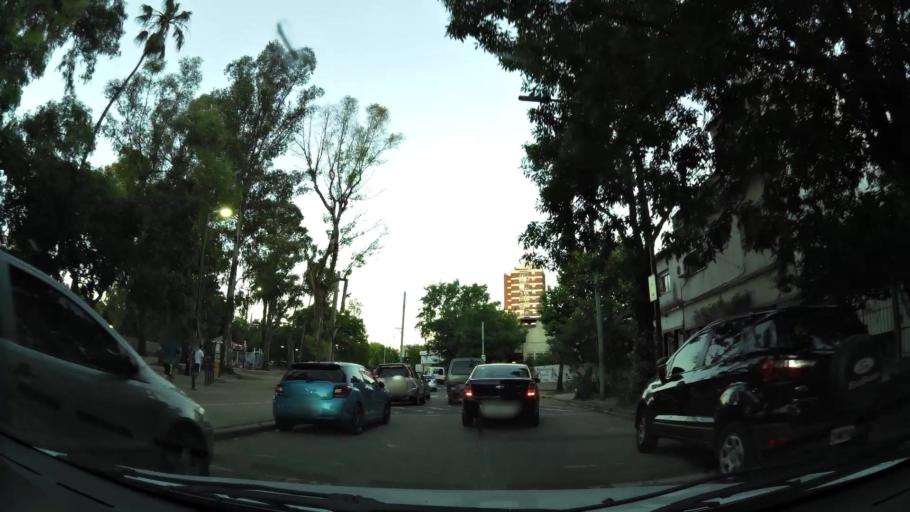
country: AR
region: Buenos Aires F.D.
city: Colegiales
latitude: -34.5513
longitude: -58.4779
